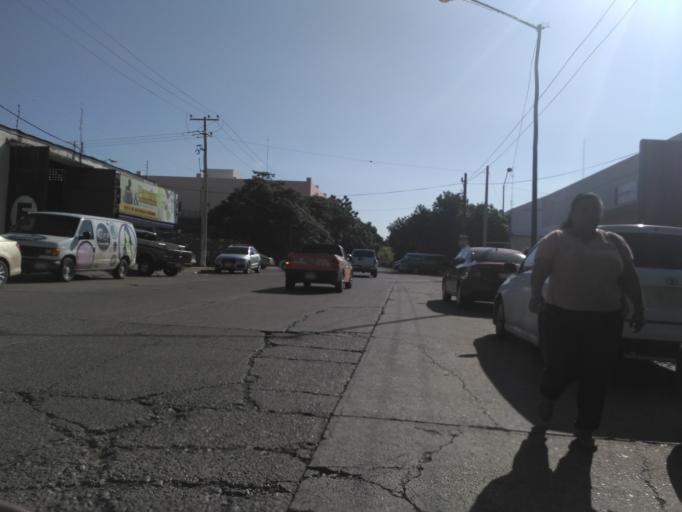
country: MX
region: Sinaloa
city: Culiacan
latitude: 24.7979
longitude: -107.4008
